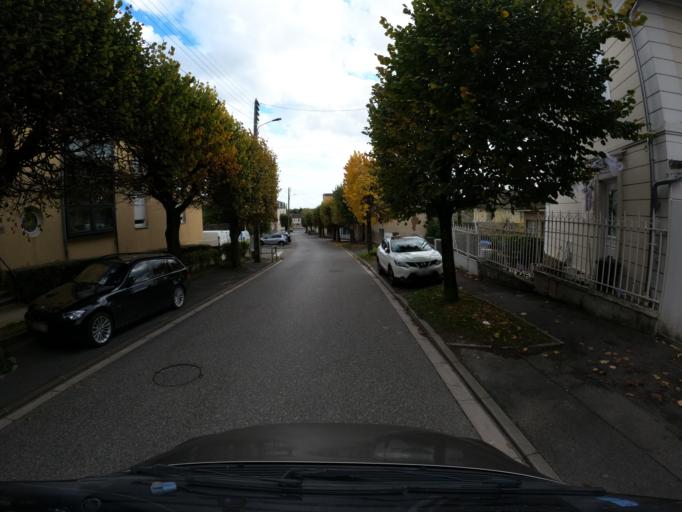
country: FR
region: Ile-de-France
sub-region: Departement de Seine-et-Marne
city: Esbly
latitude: 48.9046
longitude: 2.8101
